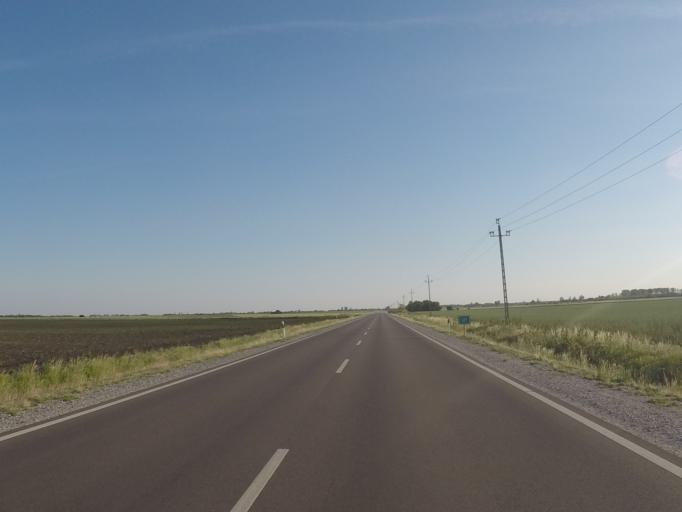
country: HU
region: Heves
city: Besenyotelek
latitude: 47.7038
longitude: 20.4052
